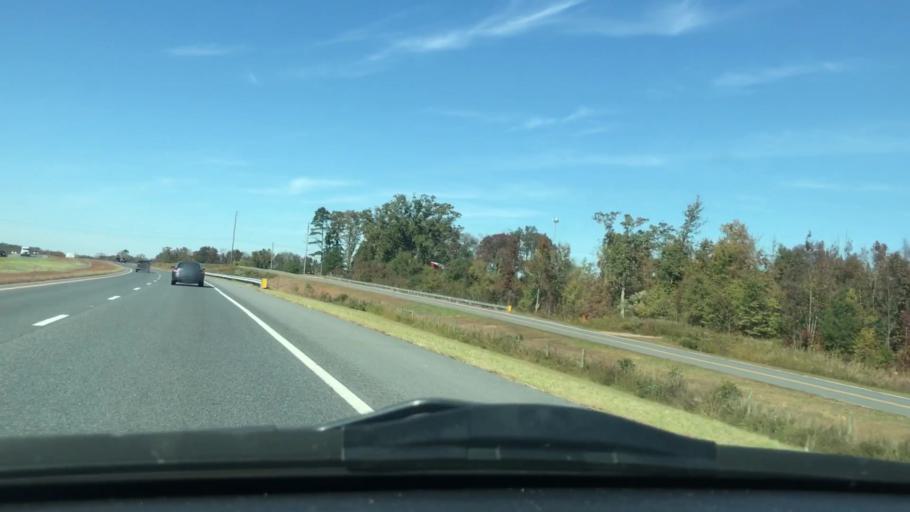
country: US
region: North Carolina
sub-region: Randolph County
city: Randleman
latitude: 35.8413
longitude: -79.8642
